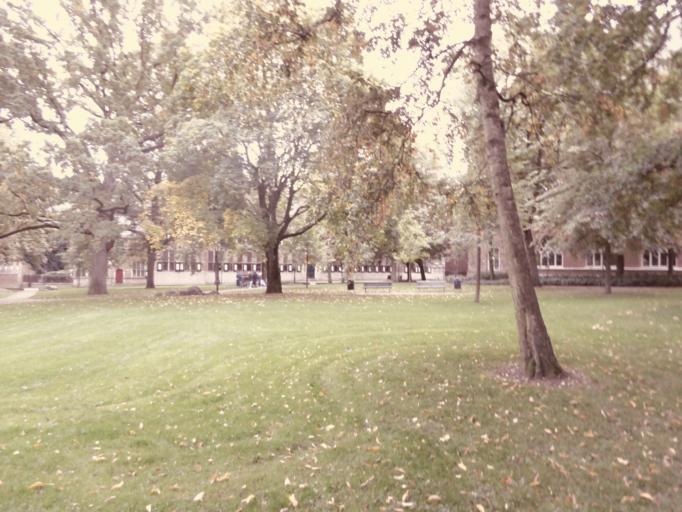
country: NL
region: Groningen
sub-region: Gemeente Groningen
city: Groningen
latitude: 53.2203
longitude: 6.5684
